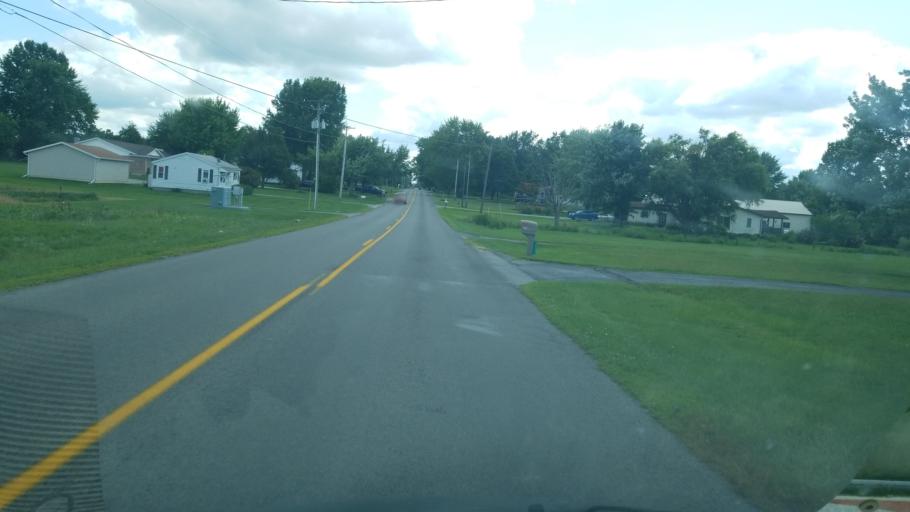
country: US
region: Ohio
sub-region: Allen County
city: Lima
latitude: 40.7683
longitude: -84.0706
